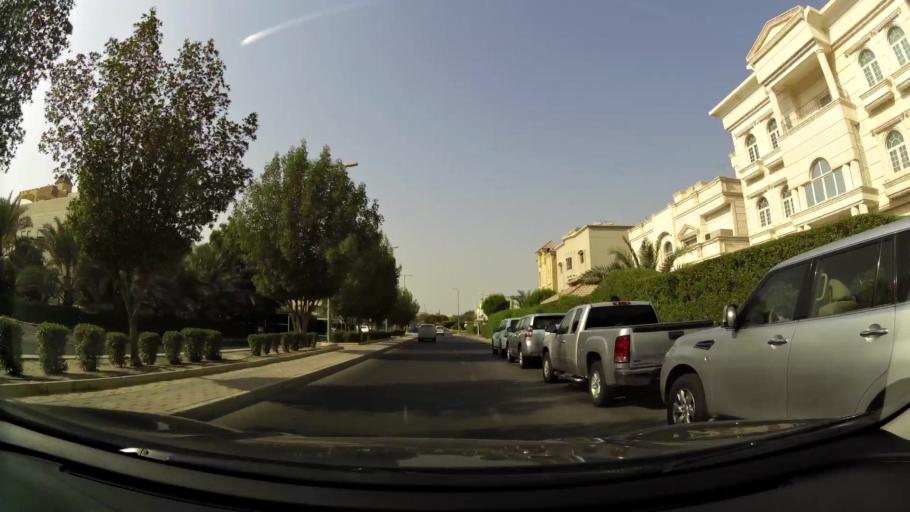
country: KW
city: Bayan
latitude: 29.2789
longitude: 48.0426
